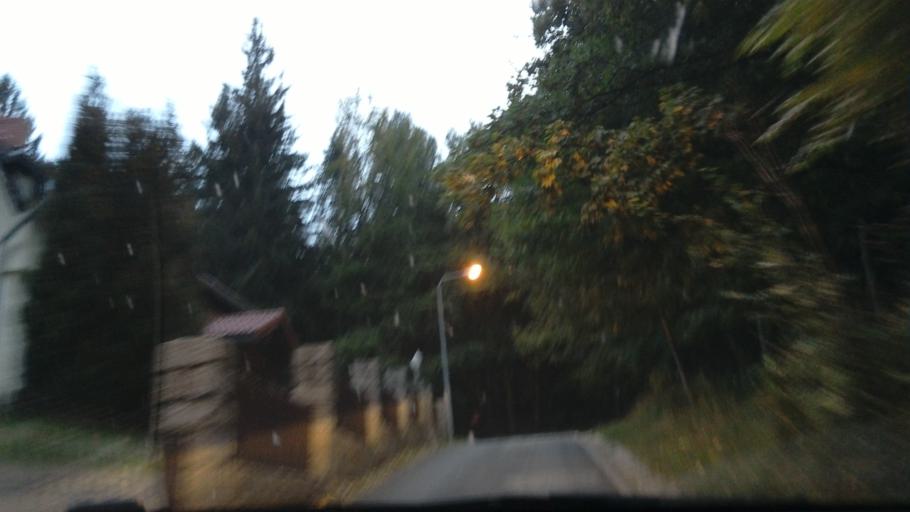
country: PL
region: Lower Silesian Voivodeship
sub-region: Powiat jeleniogorski
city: Karpacz
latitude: 50.7680
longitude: 15.7505
